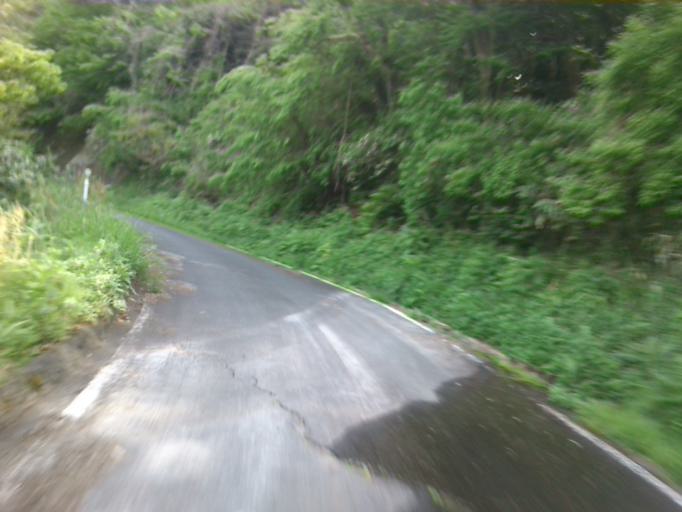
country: JP
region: Kyoto
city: Miyazu
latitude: 35.6564
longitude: 135.2369
